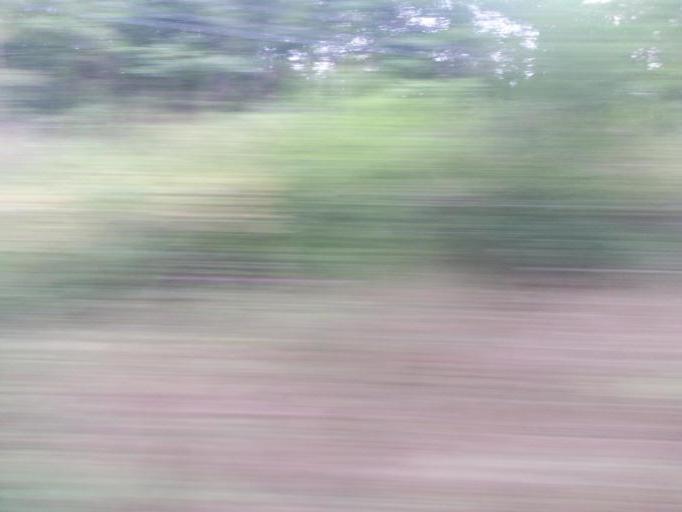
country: US
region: Tennessee
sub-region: Anderson County
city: Rocky Top
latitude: 36.1537
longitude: -84.2009
